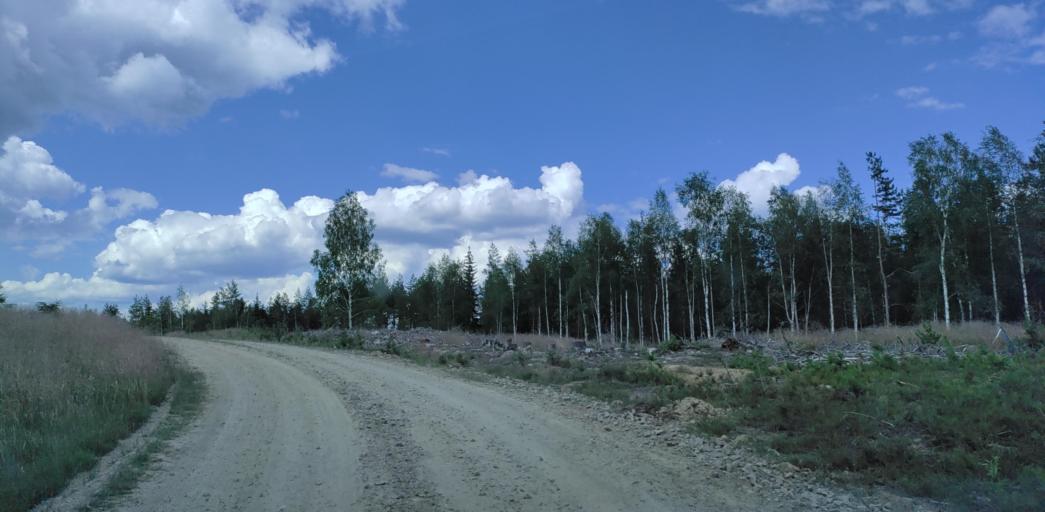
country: SE
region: Vaermland
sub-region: Hagfors Kommun
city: Ekshaerad
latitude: 60.0763
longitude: 13.3460
